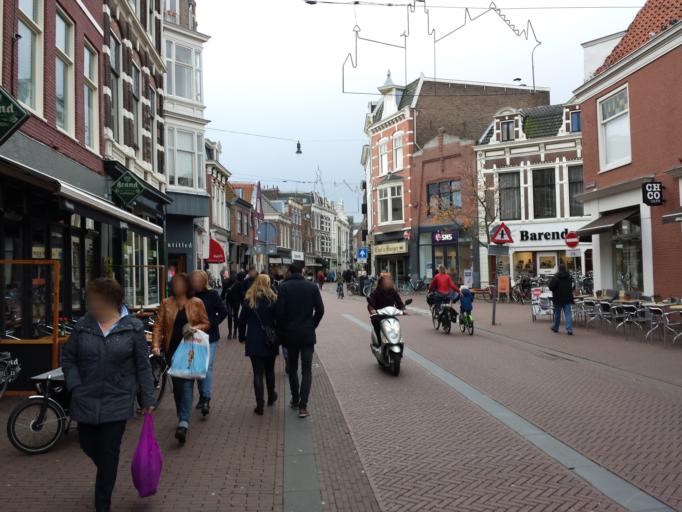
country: NL
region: North Holland
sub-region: Gemeente Haarlem
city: Haarlem
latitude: 52.3844
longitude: 4.6360
